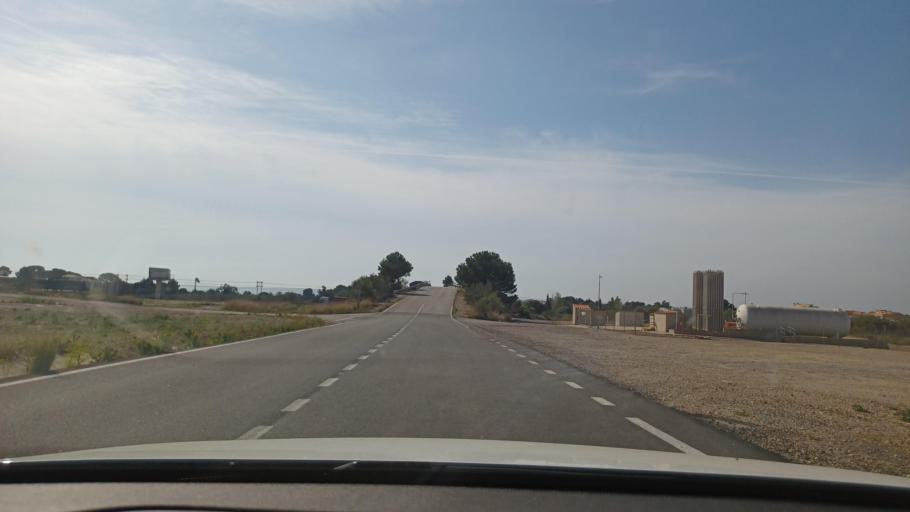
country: ES
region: Catalonia
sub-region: Provincia de Tarragona
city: L'Ampolla
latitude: 40.8198
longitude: 0.7159
